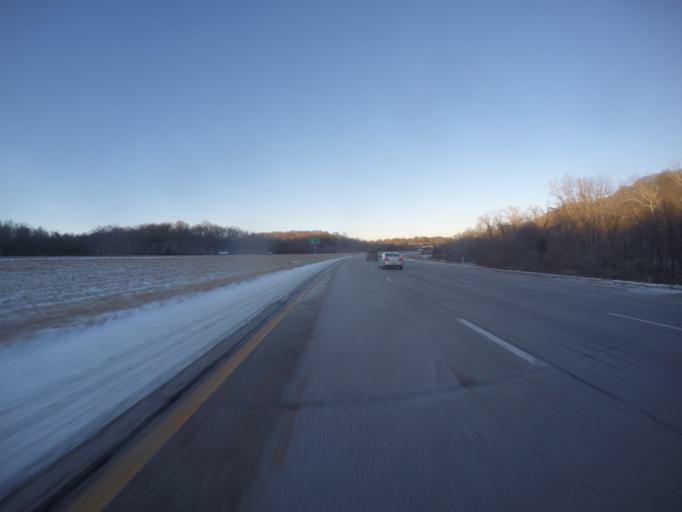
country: US
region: Kansas
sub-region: Wyandotte County
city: Edwardsville
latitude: 39.1675
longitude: -94.8131
